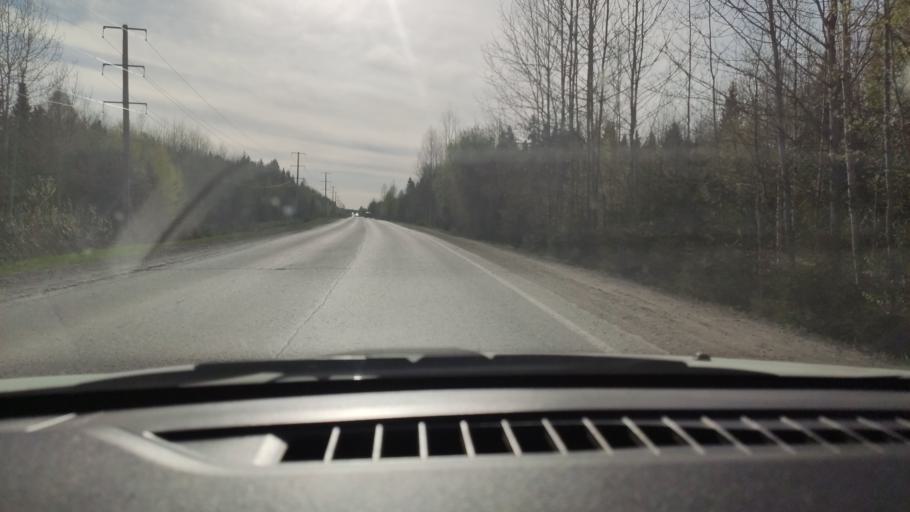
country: RU
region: Perm
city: Novyye Lyady
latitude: 57.9403
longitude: 56.6023
